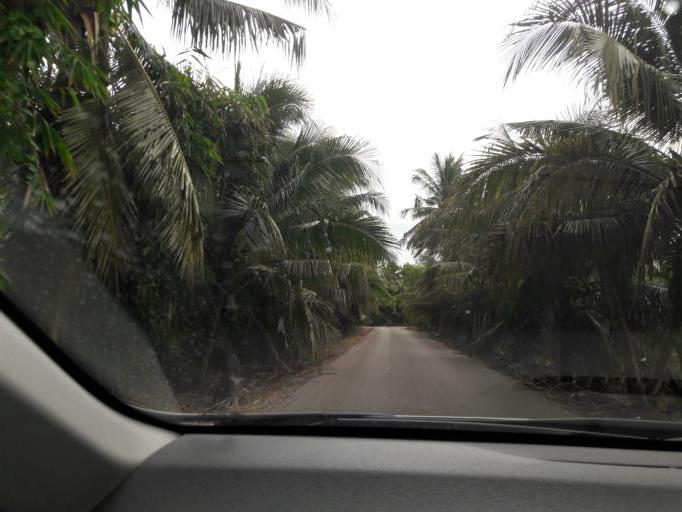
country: TH
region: Ratchaburi
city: Damnoen Saduak
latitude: 13.5481
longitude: 99.9974
